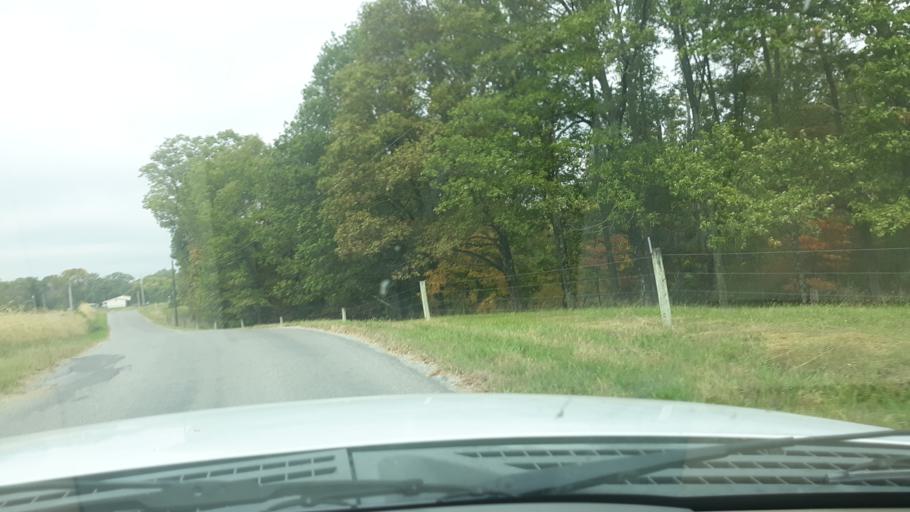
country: US
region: Illinois
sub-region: Saline County
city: Eldorado
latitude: 37.8369
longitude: -88.4859
